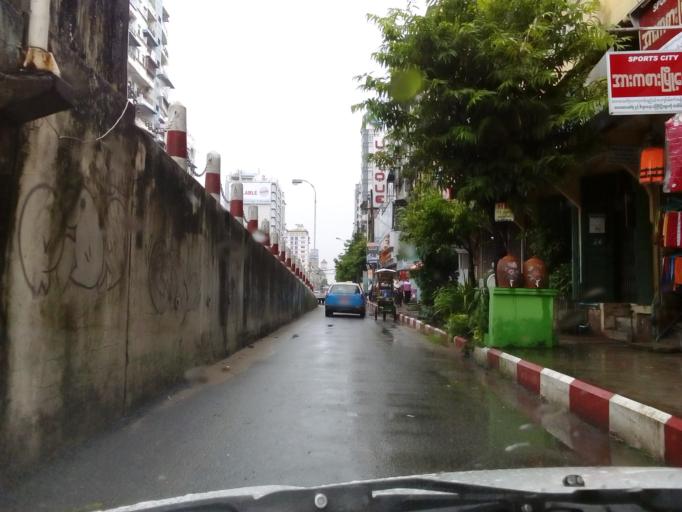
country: MM
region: Yangon
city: Yangon
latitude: 16.7783
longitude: 96.1617
